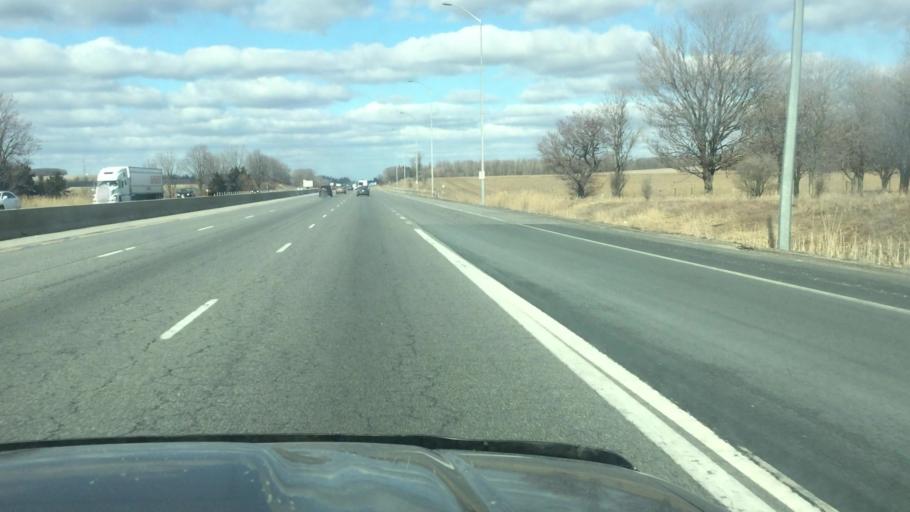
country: CA
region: Ontario
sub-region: Oxford County
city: Woodstock
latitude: 43.0691
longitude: -80.7957
